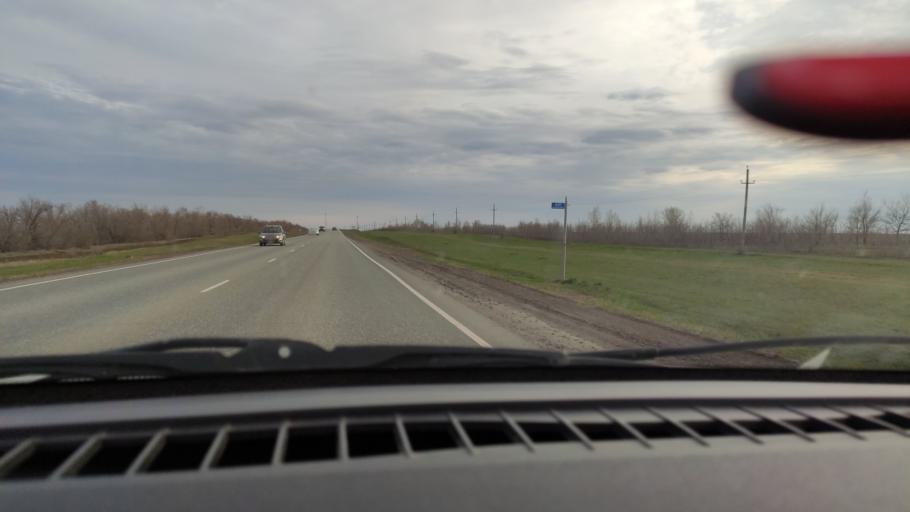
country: RU
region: Orenburg
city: Tatarskaya Kargala
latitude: 51.9985
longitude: 55.1962
